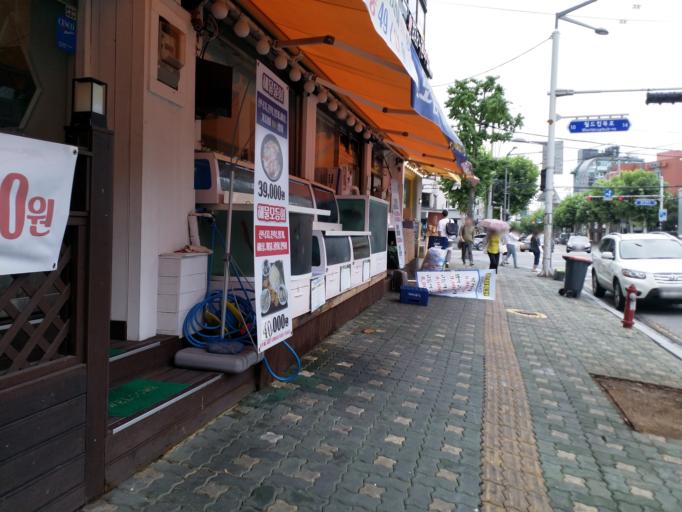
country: KR
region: Seoul
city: Seoul
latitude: 37.5561
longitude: 126.9211
